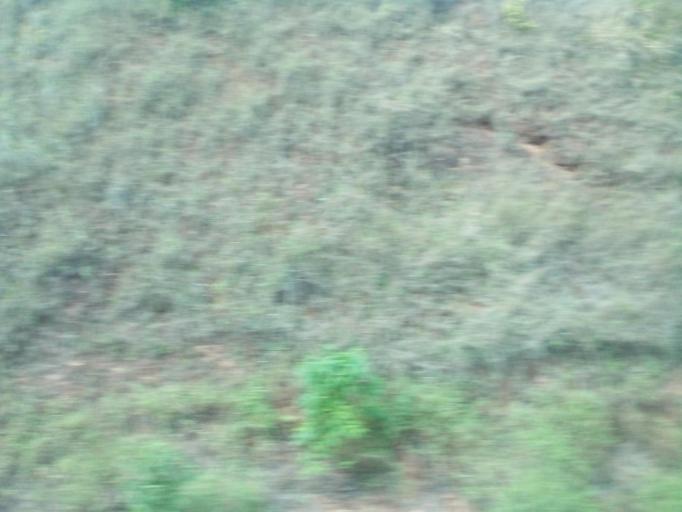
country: BR
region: Minas Gerais
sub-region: Caete
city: Caete
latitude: -19.9081
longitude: -43.7146
